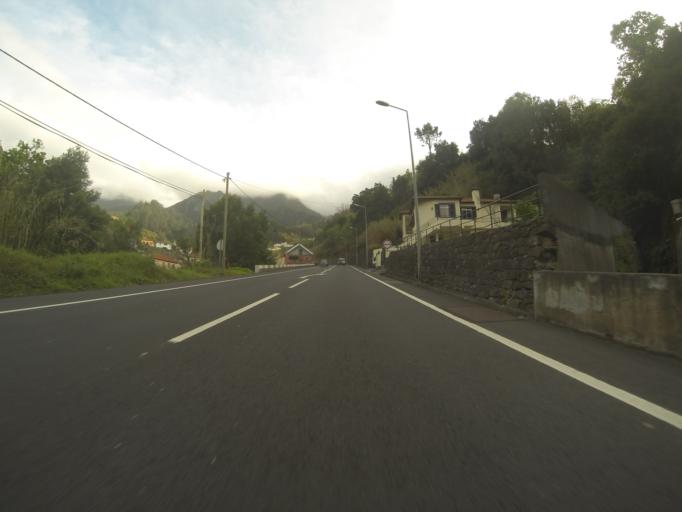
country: PT
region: Madeira
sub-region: Sao Vicente
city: Sao Vicente
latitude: 32.7784
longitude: -17.0332
